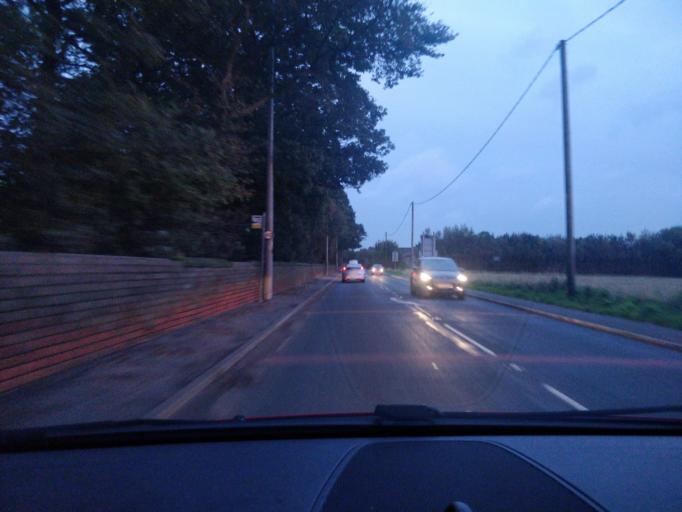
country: GB
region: England
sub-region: Lancashire
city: Ormskirk
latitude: 53.6044
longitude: -2.9325
